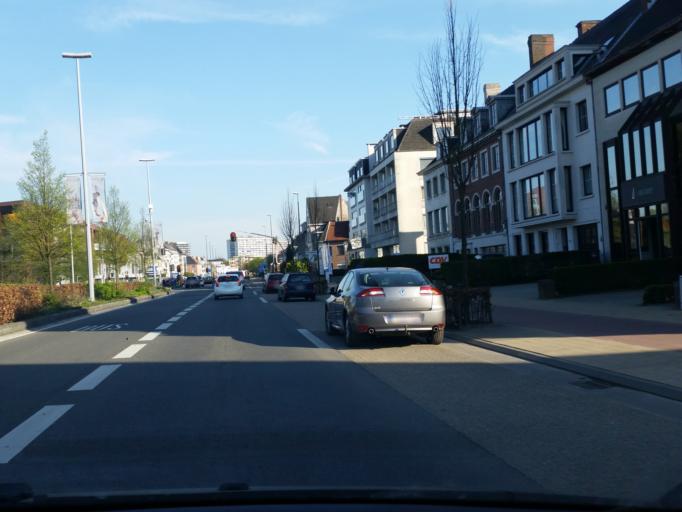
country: BE
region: Flanders
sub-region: Provincie Oost-Vlaanderen
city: Sint-Niklaas
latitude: 51.1608
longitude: 4.1471
